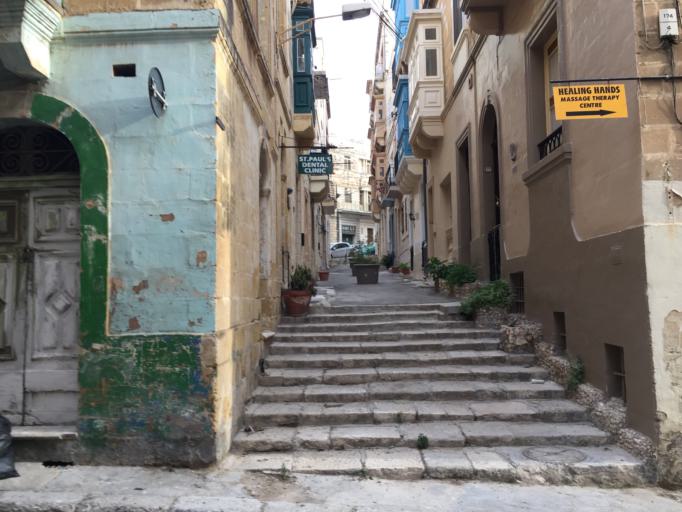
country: MT
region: L-Isla
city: Senglea
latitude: 35.8818
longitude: 14.5188
